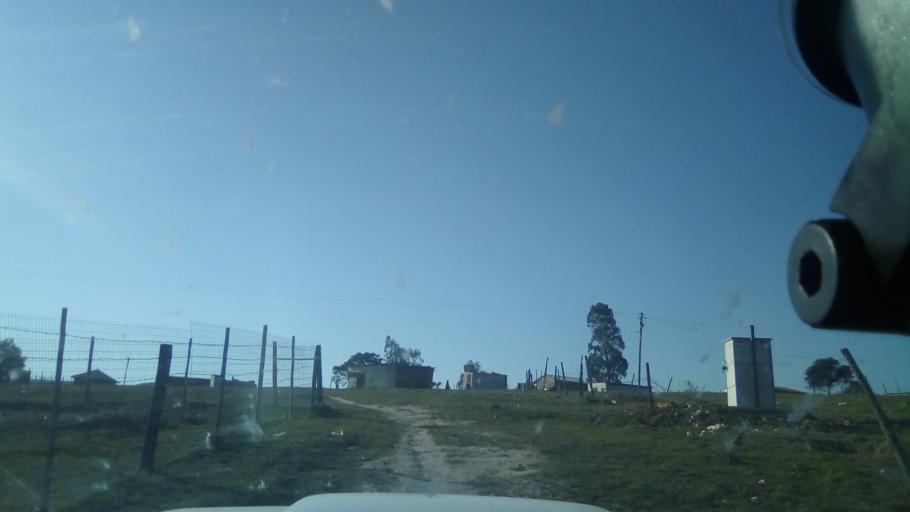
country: ZA
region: Eastern Cape
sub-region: Buffalo City Metropolitan Municipality
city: Bhisho
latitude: -32.9885
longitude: 27.2686
